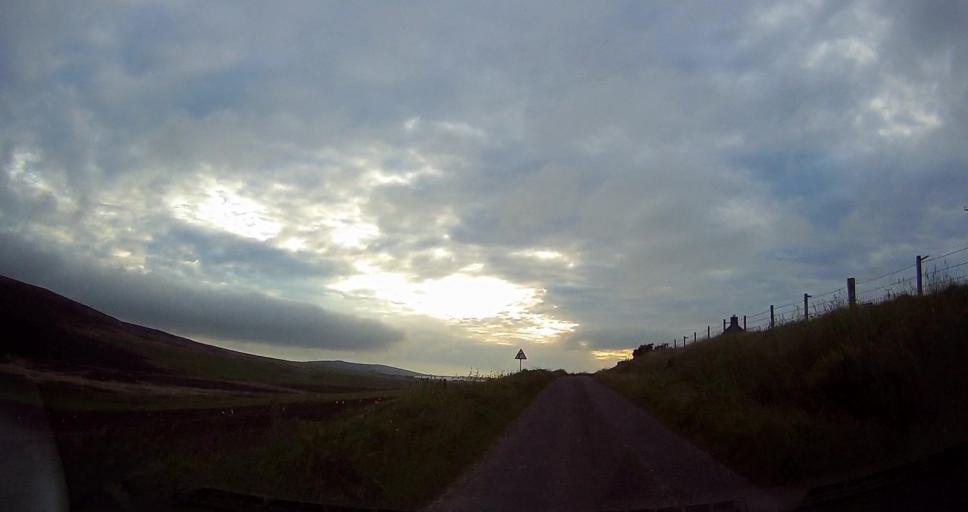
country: GB
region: Scotland
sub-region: Orkney Islands
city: Stromness
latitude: 59.1010
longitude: -3.2077
